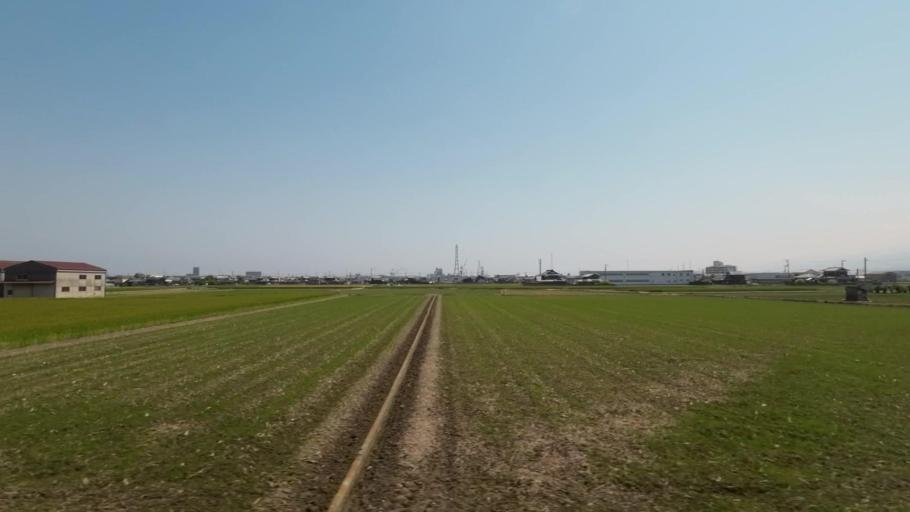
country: JP
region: Ehime
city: Saijo
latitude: 33.9212
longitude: 133.0932
